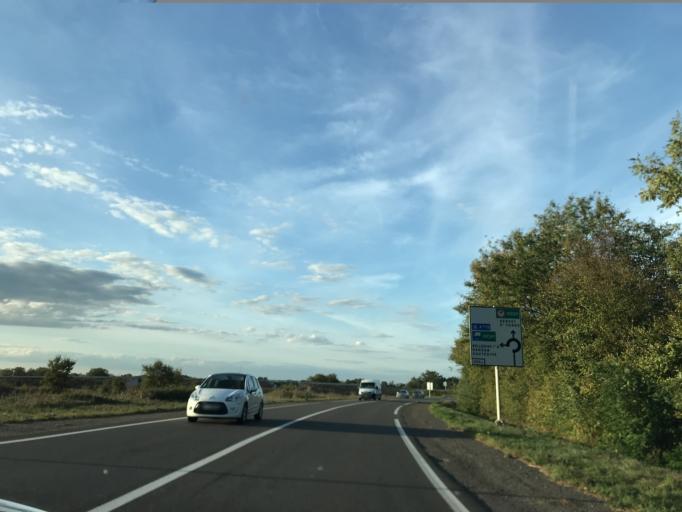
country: FR
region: Auvergne
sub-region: Departement de l'Allier
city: Saint-Yorre
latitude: 46.0428
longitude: 3.4730
